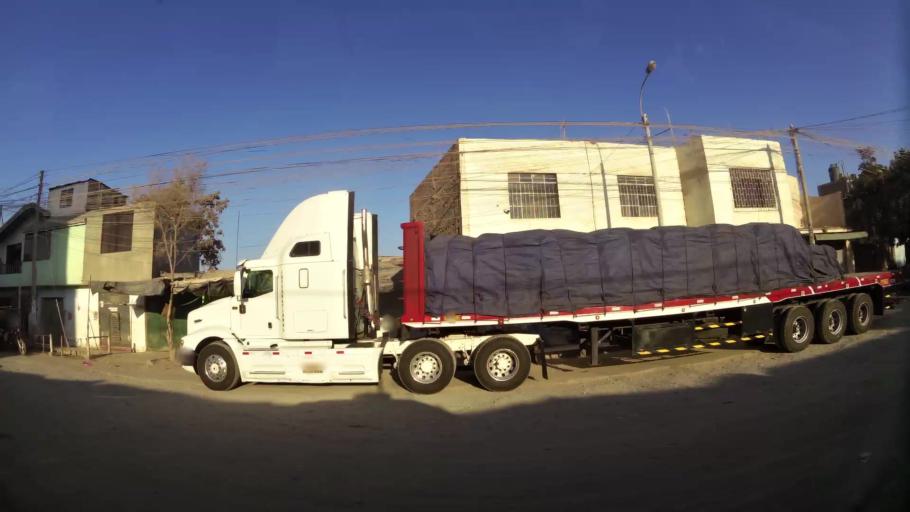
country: PE
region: Ica
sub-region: Provincia de Ica
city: Ica
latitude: -14.0613
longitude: -75.7352
